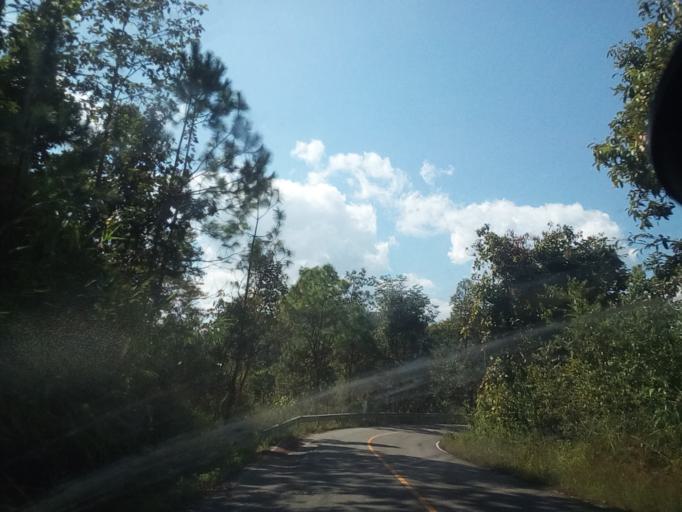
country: TH
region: Chiang Mai
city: Samoeng
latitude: 18.8760
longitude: 98.6831
